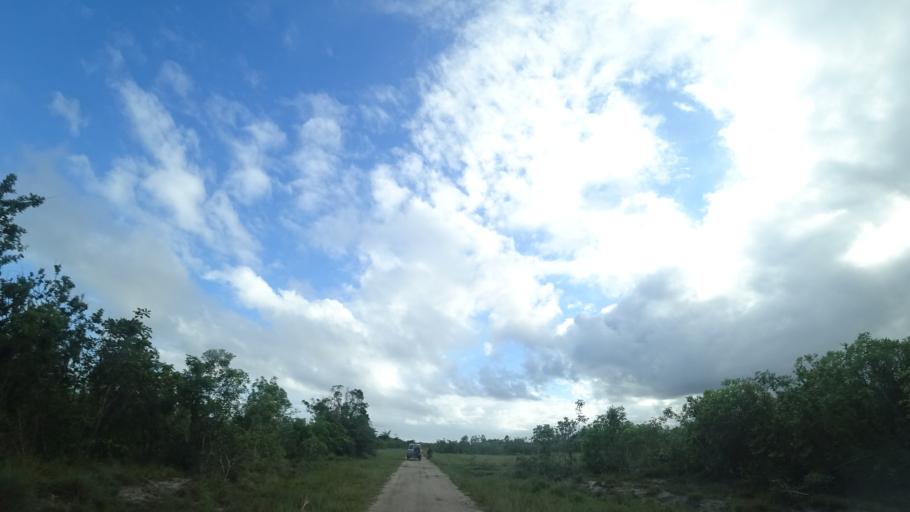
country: MZ
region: Sofala
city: Beira
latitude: -19.6707
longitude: 35.0586
